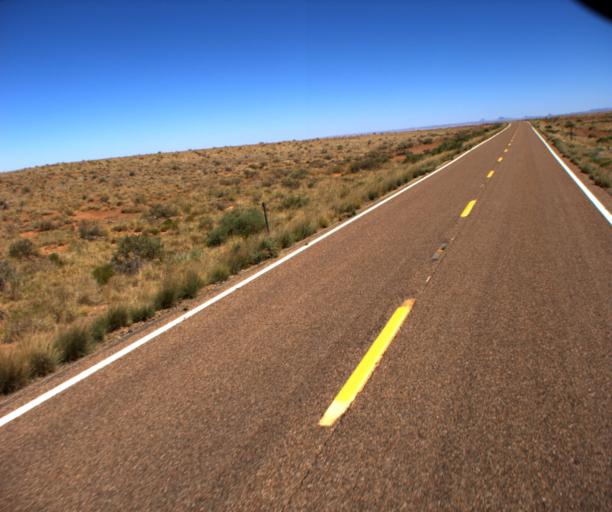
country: US
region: Arizona
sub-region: Navajo County
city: Winslow
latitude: 34.9071
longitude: -110.6401
